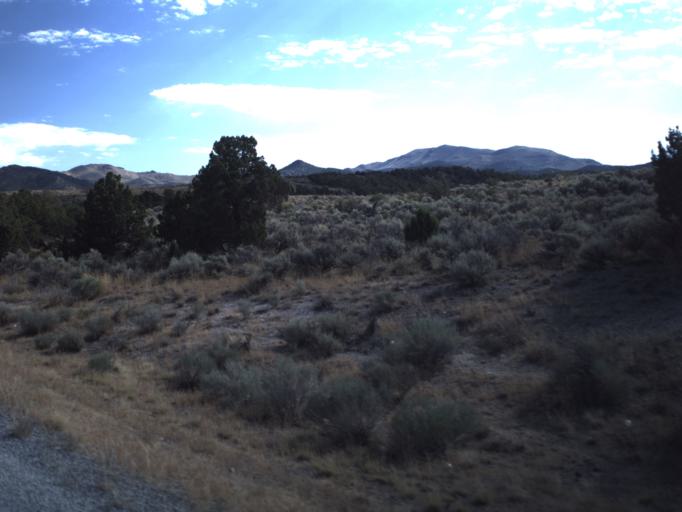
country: US
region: Utah
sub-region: Juab County
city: Mona
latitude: 39.7804
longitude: -112.1524
